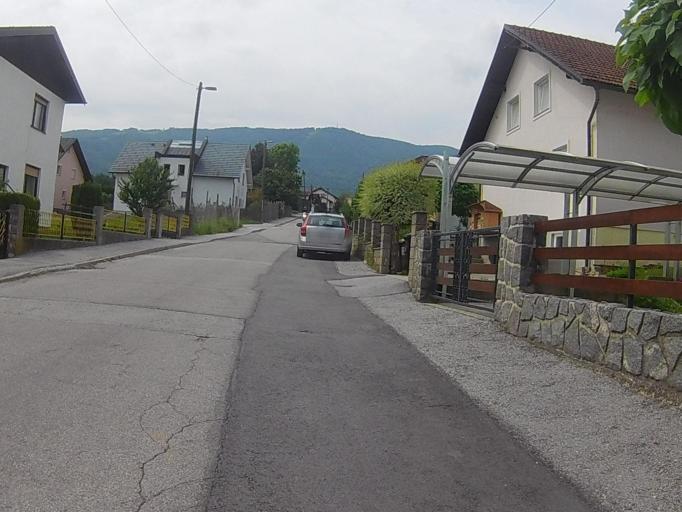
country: SI
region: Maribor
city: Pekre
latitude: 46.5468
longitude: 15.5962
